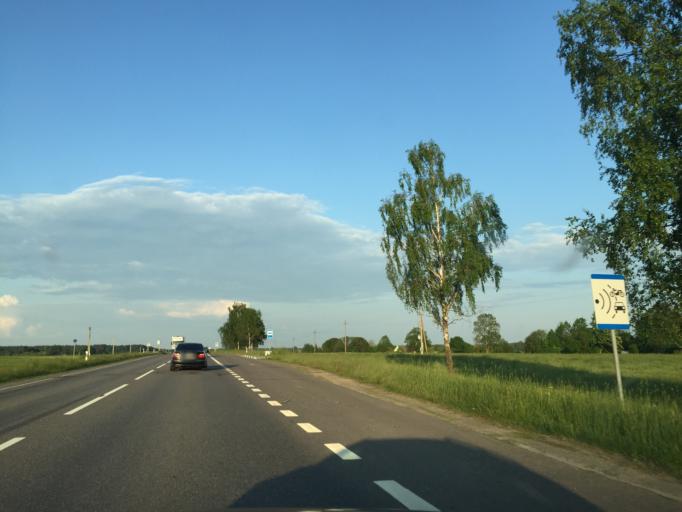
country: LT
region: Telsiu apskritis
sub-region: Telsiai
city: Telsiai
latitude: 56.0012
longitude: 22.4525
